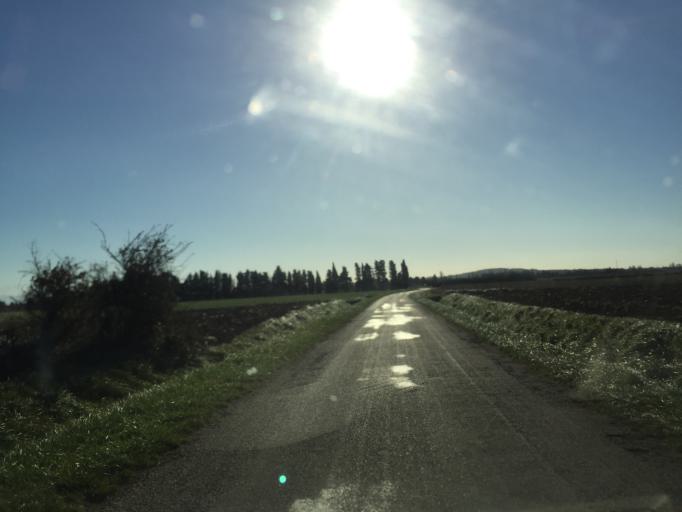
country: FR
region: Provence-Alpes-Cote d'Azur
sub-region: Departement du Vaucluse
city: Bedarrides
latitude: 44.0683
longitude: 4.9075
